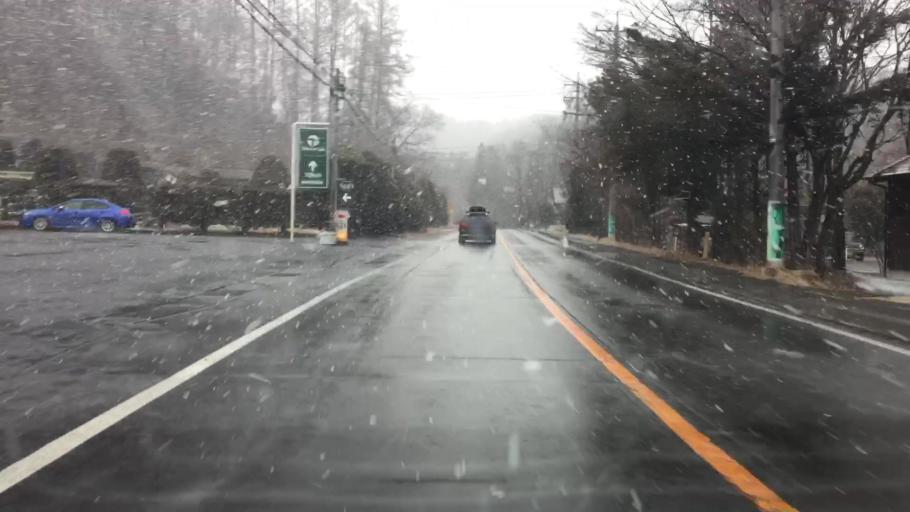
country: JP
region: Nagano
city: Komoro
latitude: 36.3559
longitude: 138.5897
